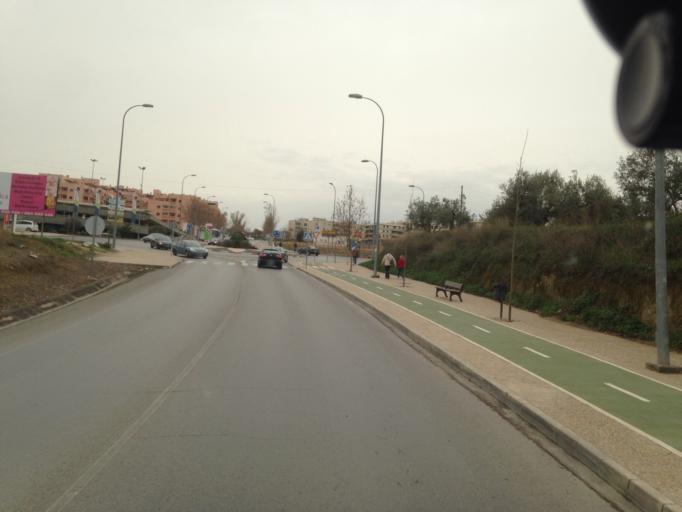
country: ES
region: Andalusia
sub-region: Provincia de Malaga
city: Antequera
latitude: 37.0262
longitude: -4.5749
